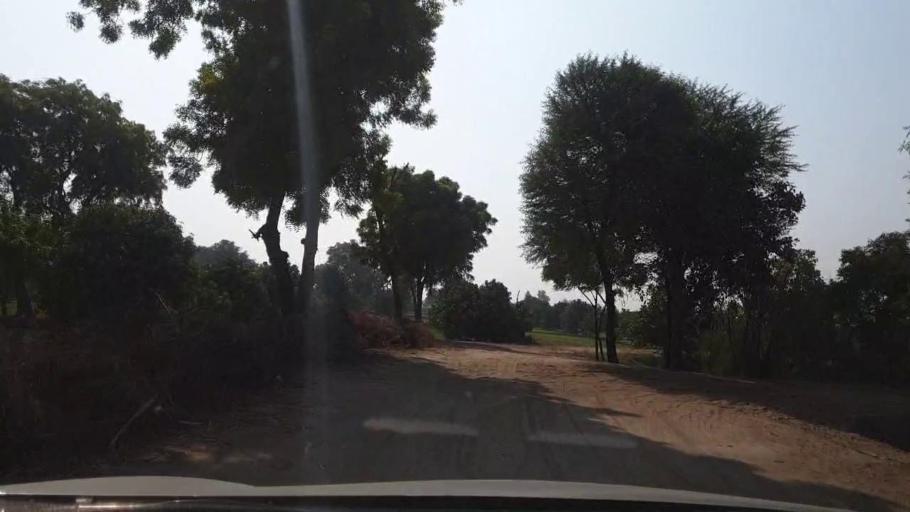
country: PK
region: Sindh
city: Tando Allahyar
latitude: 25.5307
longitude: 68.7686
